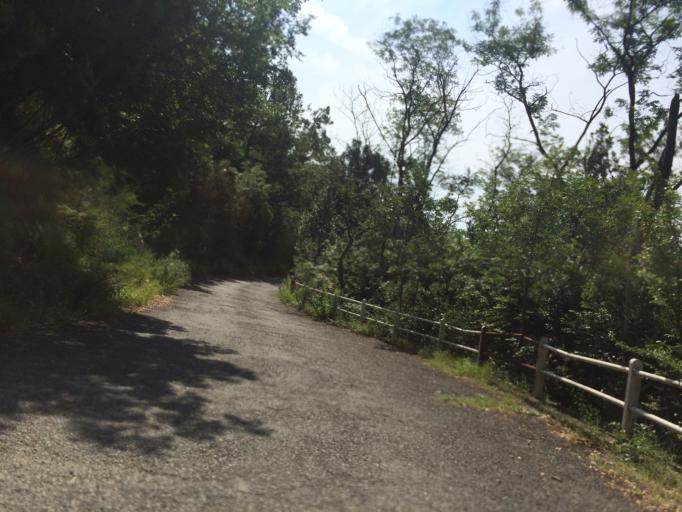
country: IT
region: Liguria
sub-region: Provincia di Genova
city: Sciarborasca
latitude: 44.4051
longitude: 8.5763
